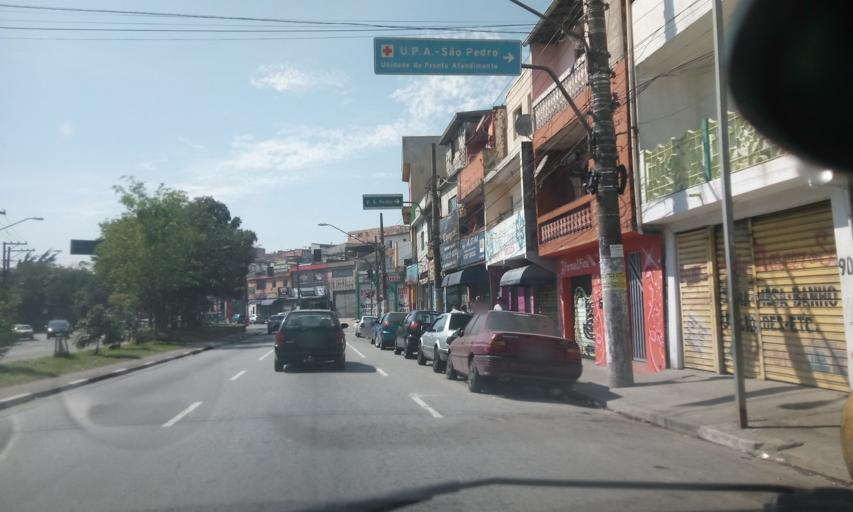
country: BR
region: Sao Paulo
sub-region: Sao Bernardo Do Campo
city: Sao Bernardo do Campo
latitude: -23.7132
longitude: -46.5307
